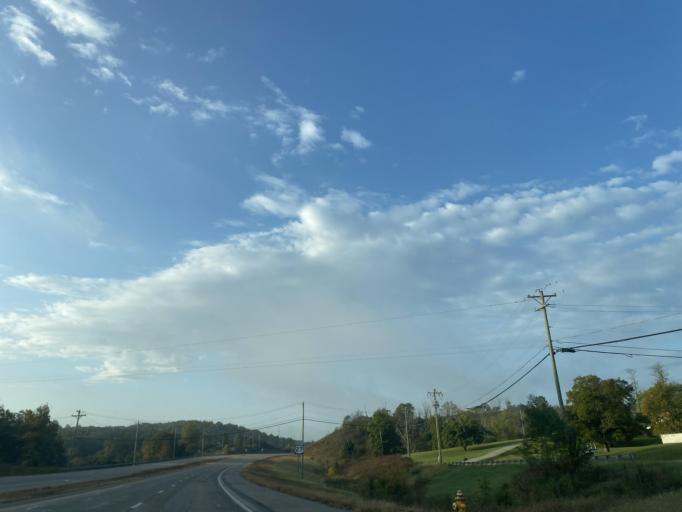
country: US
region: Kentucky
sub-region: Campbell County
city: Claryville
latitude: 38.8827
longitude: -84.3877
